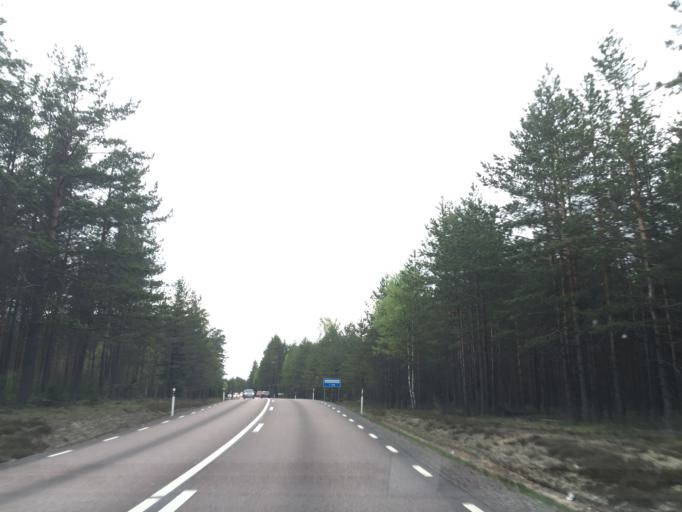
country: SE
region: Vaermland
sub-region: Eda Kommun
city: Charlottenberg
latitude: 59.9021
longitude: 12.2793
